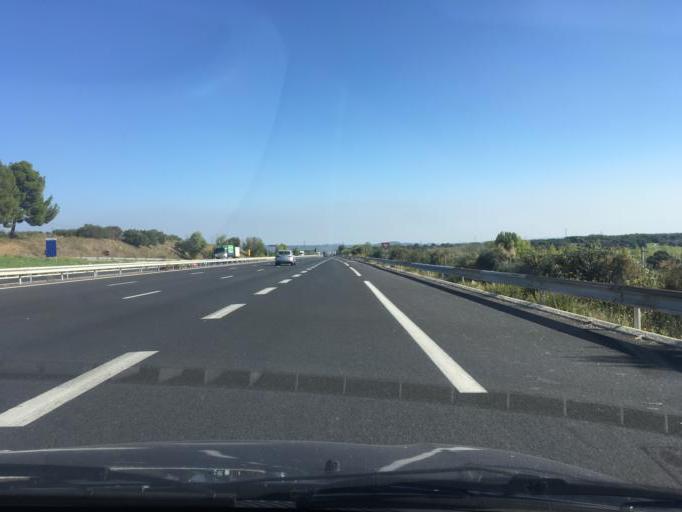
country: FR
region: Languedoc-Roussillon
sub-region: Departement du Gard
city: Sernhac
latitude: 43.9020
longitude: 4.5344
